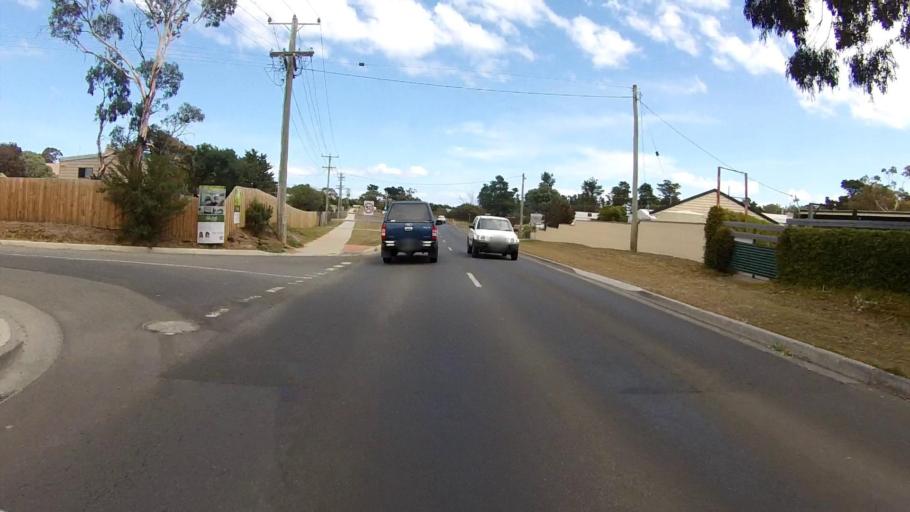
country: AU
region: Tasmania
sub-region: Sorell
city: Sorell
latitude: -42.8584
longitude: 147.6156
